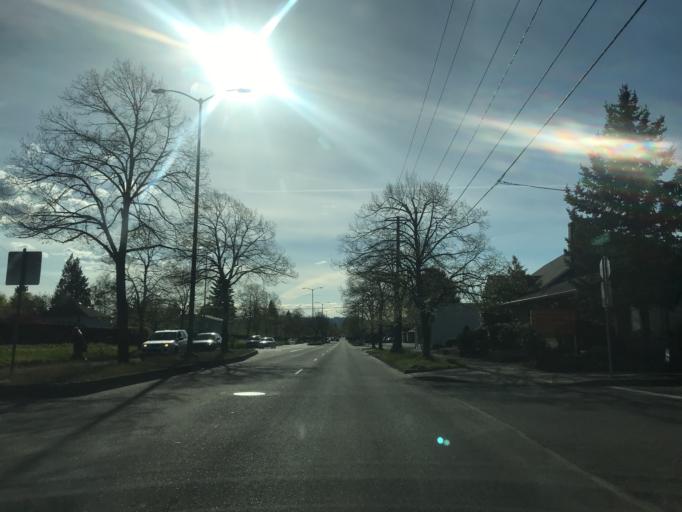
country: US
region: Oregon
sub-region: Multnomah County
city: Lents
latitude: 45.4975
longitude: -122.5983
